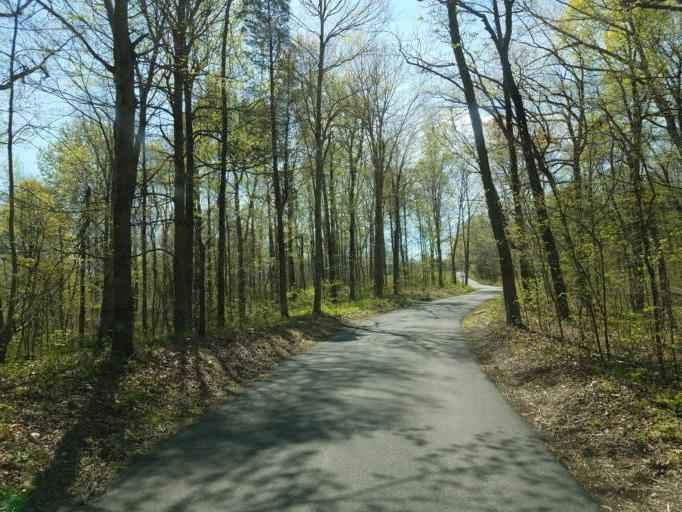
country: US
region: Kentucky
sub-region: Barren County
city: Cave City
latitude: 37.1753
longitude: -86.0437
